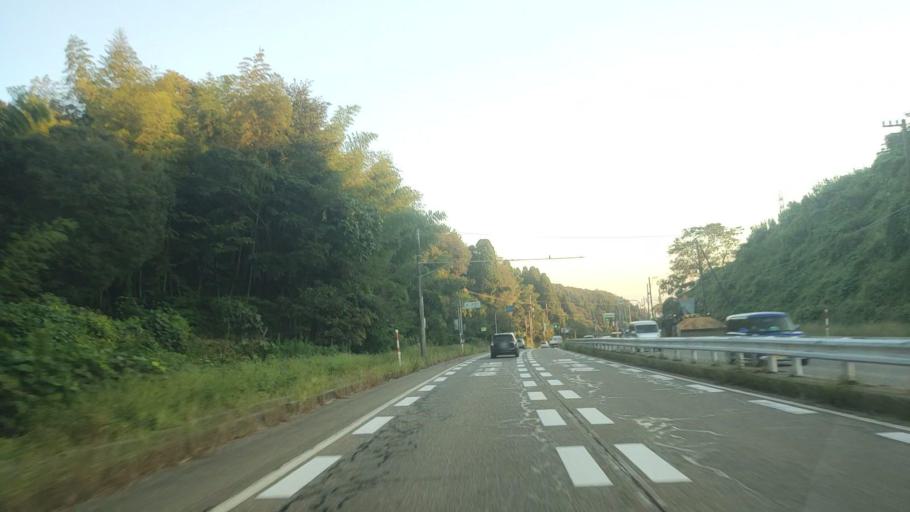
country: JP
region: Toyama
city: Takaoka
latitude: 36.7953
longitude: 137.0021
